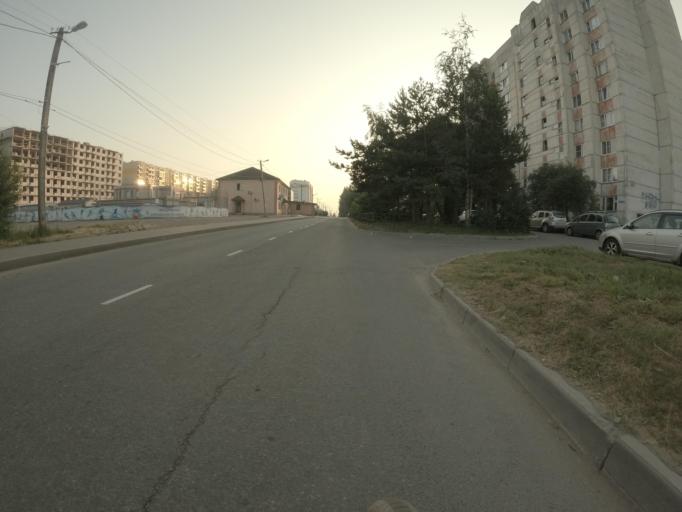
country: RU
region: St.-Petersburg
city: Pontonnyy
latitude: 59.7973
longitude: 30.6353
